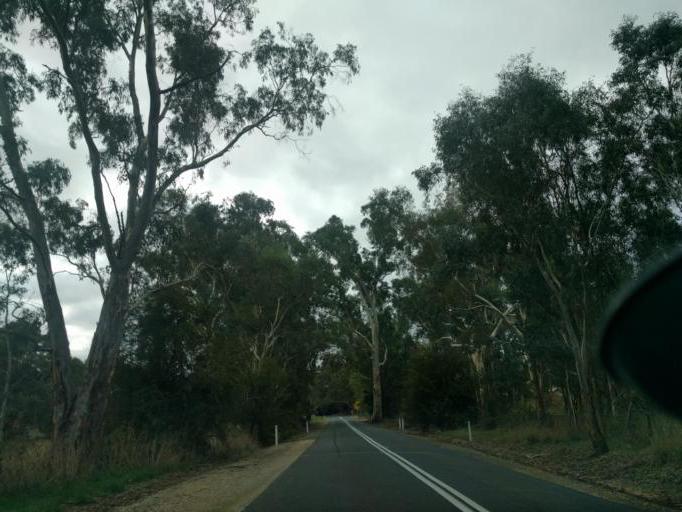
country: AU
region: South Australia
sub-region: Mount Barker
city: Hahndorf
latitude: -35.0740
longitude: 138.7781
